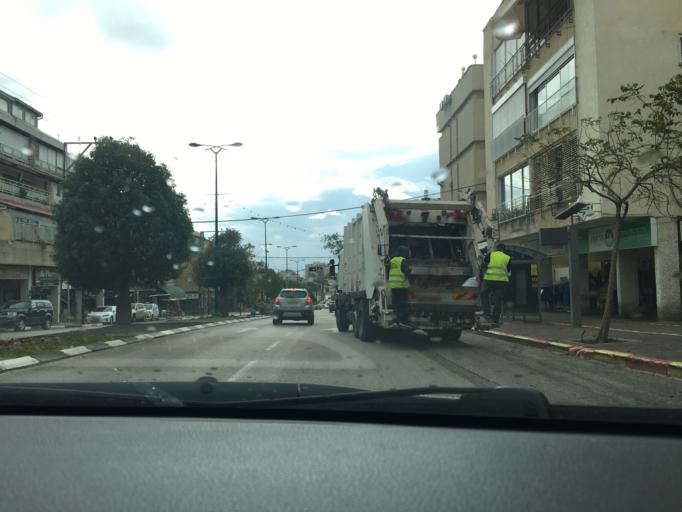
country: IL
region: Tel Aviv
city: Ramat HaSharon
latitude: 32.1417
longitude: 34.8430
